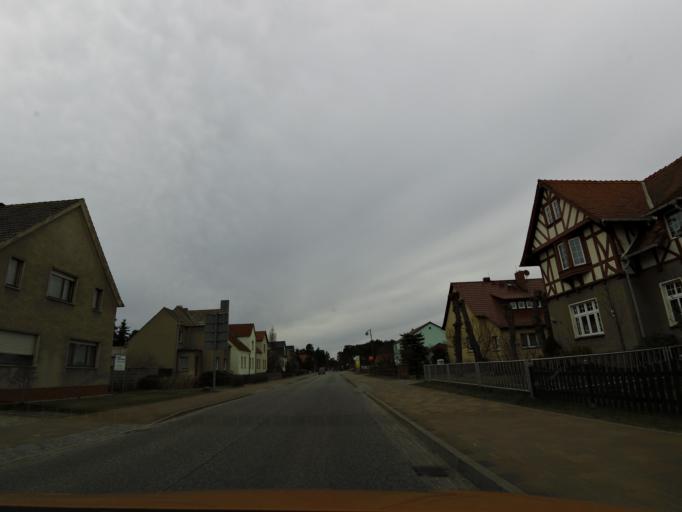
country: DE
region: Brandenburg
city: Bruck
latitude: 52.1807
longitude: 12.7570
